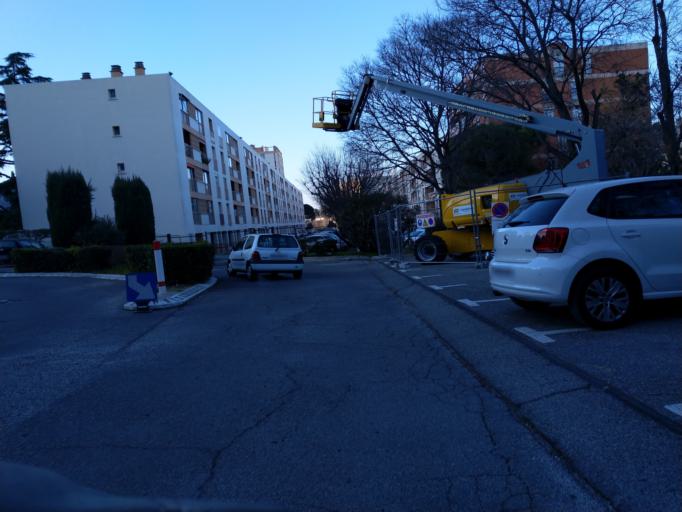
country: FR
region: Provence-Alpes-Cote d'Azur
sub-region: Departement des Bouches-du-Rhone
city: Marseille 10
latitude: 43.2724
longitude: 5.4313
